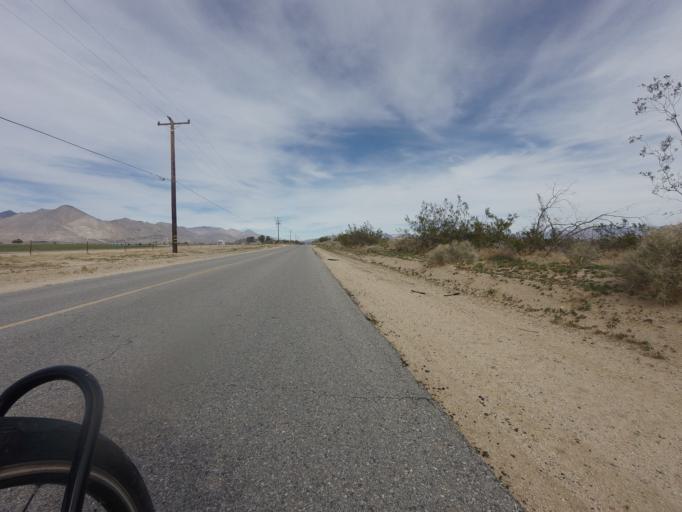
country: US
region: California
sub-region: Kern County
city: Inyokern
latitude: 35.7420
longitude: -117.8403
